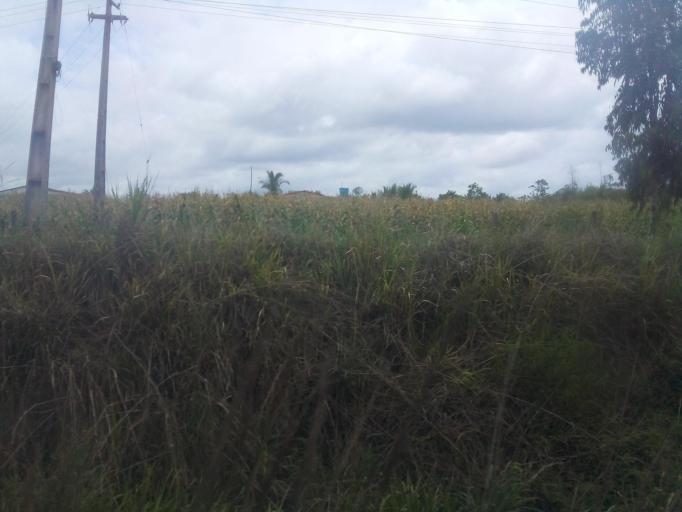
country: BR
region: Maranhao
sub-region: Santa Ines
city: Santa Ines
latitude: -3.6538
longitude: -45.7839
